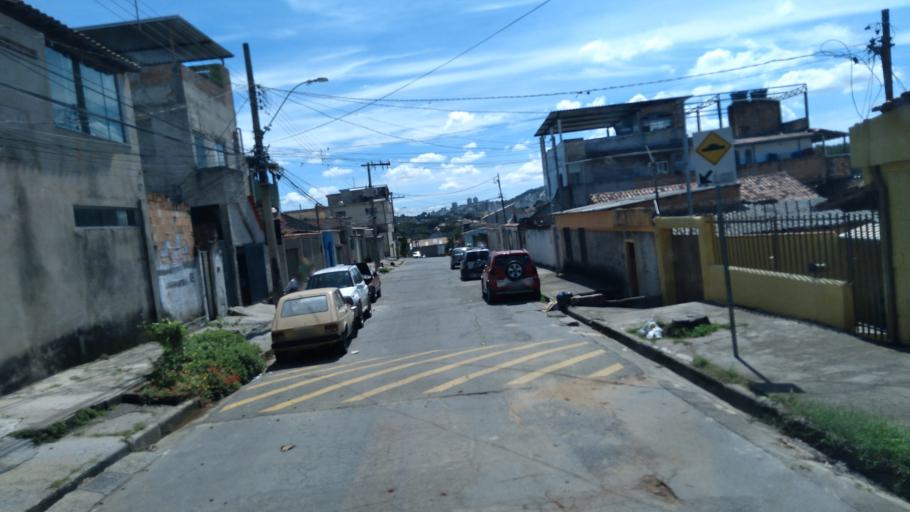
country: BR
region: Minas Gerais
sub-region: Contagem
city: Contagem
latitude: -19.8933
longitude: -44.0123
